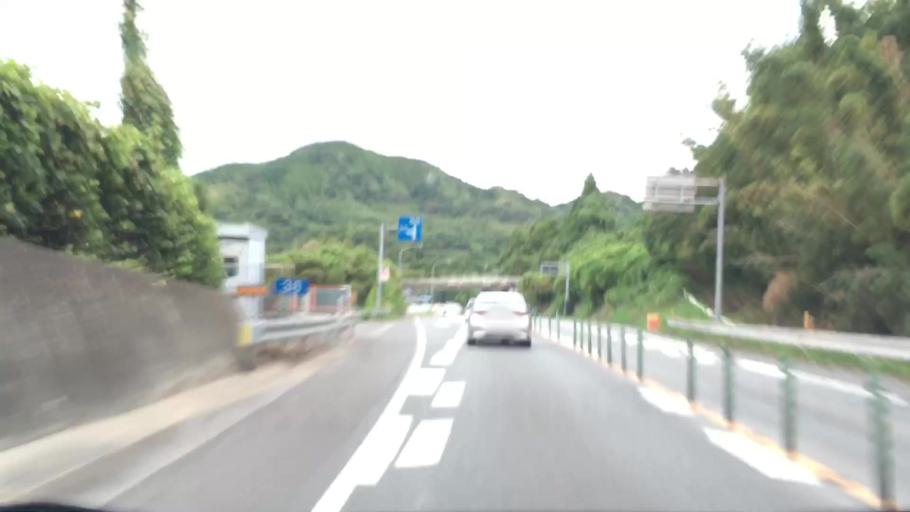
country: JP
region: Saga Prefecture
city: Karatsu
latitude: 33.4822
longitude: 130.0511
